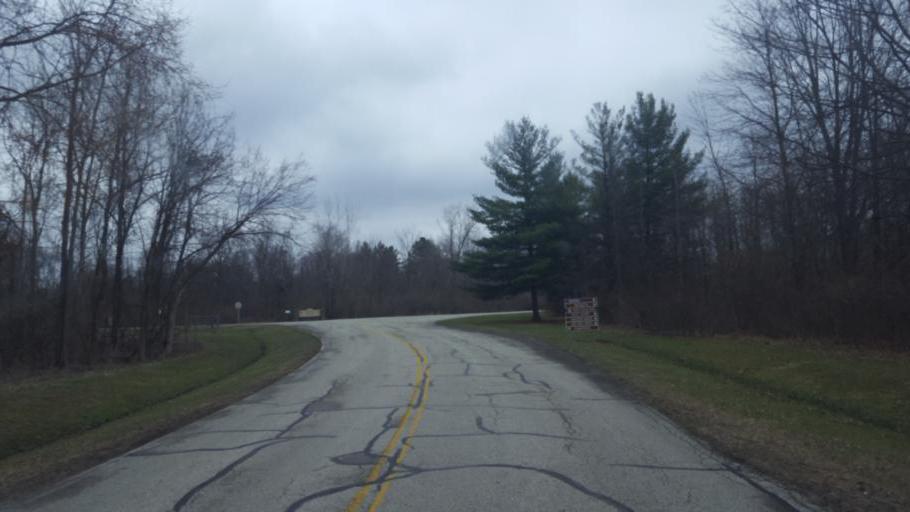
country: US
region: Ohio
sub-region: Delaware County
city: Delaware
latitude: 40.3783
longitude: -83.0656
